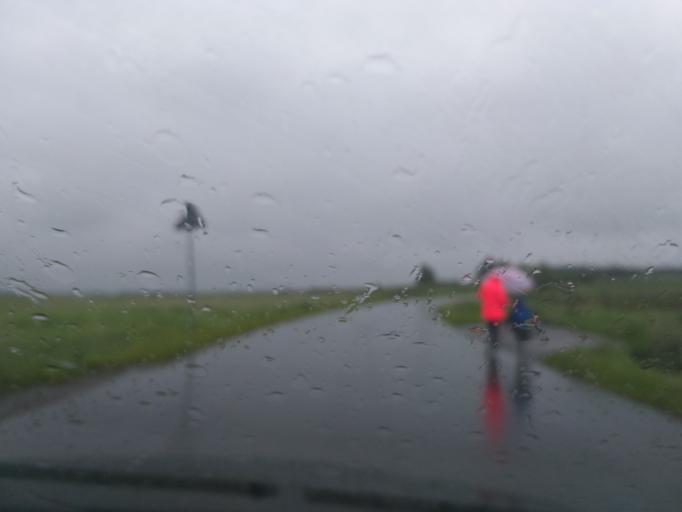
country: PL
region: Subcarpathian Voivodeship
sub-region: Powiat jasielski
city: Debowiec
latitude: 49.6696
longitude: 21.4526
